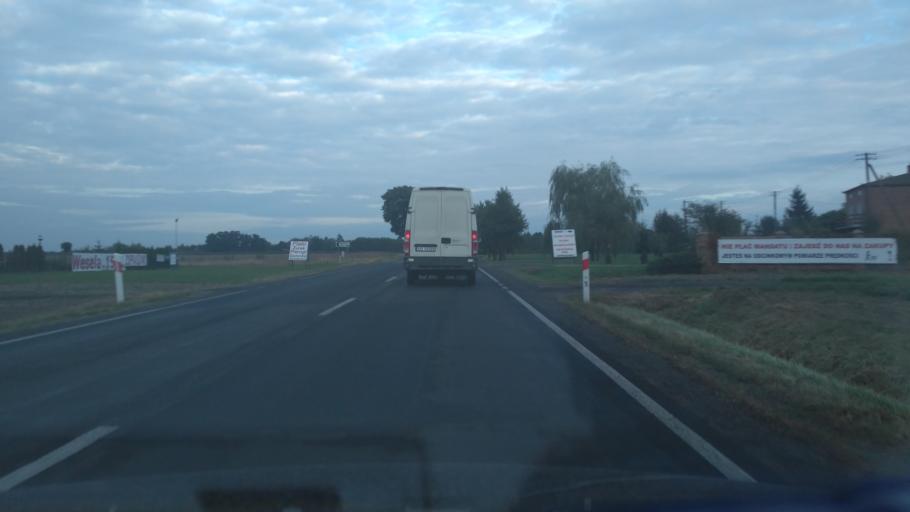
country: PL
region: Lublin Voivodeship
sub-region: Powiat leczynski
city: Spiczyn
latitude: 51.2993
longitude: 22.7632
